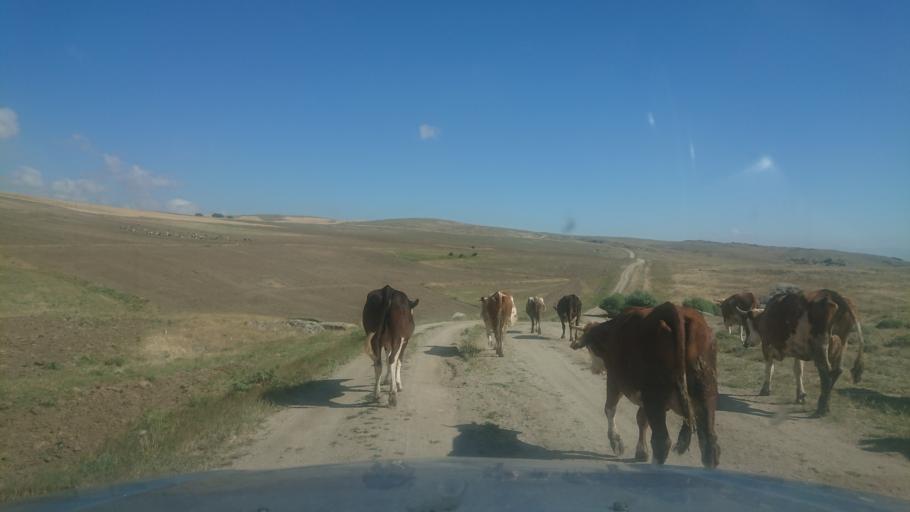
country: TR
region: Aksaray
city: Agacoren
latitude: 38.9121
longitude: 33.8555
